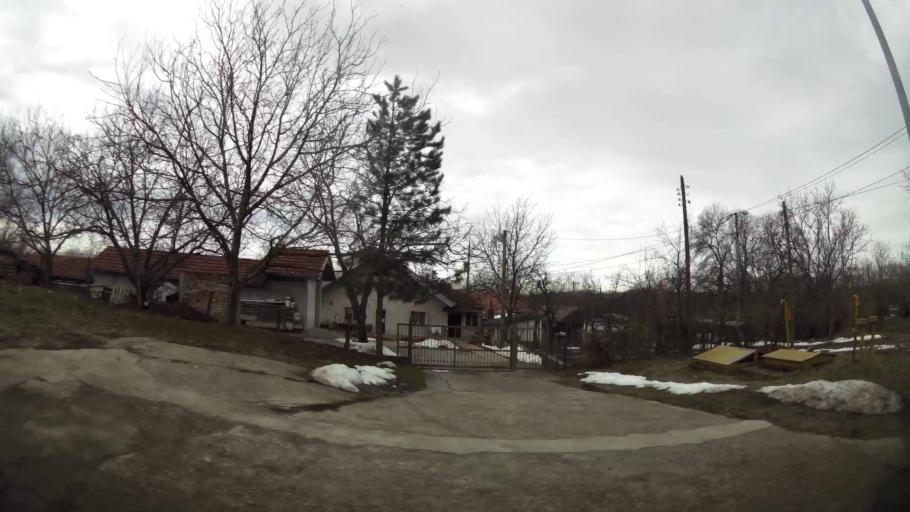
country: RS
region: Central Serbia
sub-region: Belgrade
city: Cukarica
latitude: 44.7603
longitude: 20.4037
